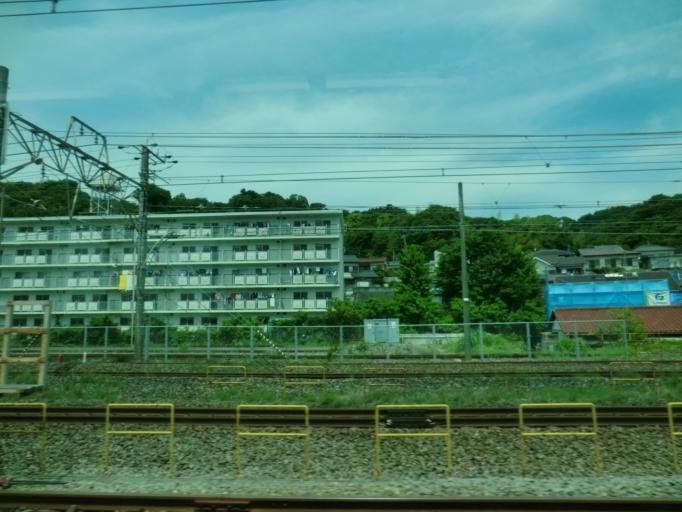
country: JP
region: Kanagawa
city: Ninomiya
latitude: 35.2831
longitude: 139.2205
